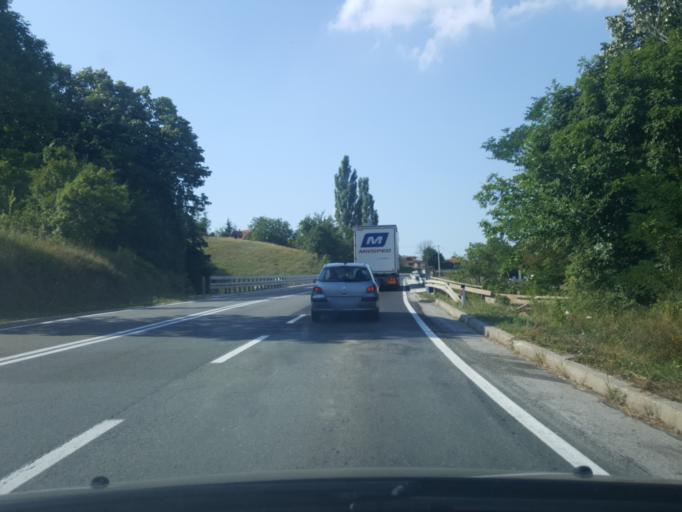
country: RS
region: Central Serbia
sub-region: Moravicki Okrug
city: Gornji Milanovac
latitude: 44.1179
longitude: 20.4829
